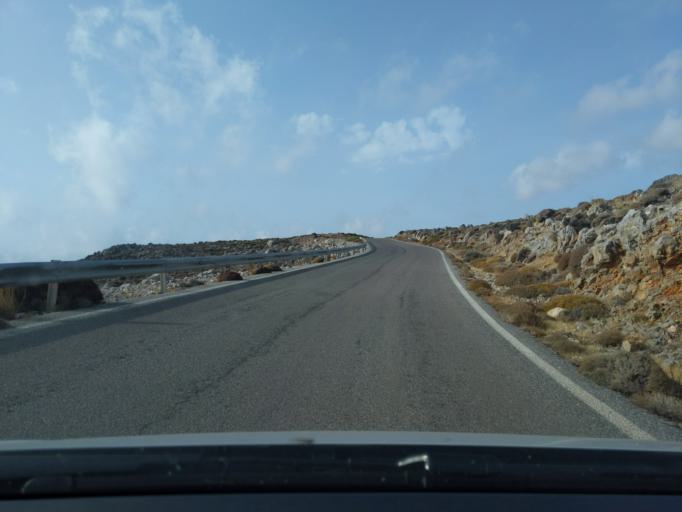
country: GR
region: Crete
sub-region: Nomos Lasithiou
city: Palekastro
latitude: 35.0881
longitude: 26.2673
